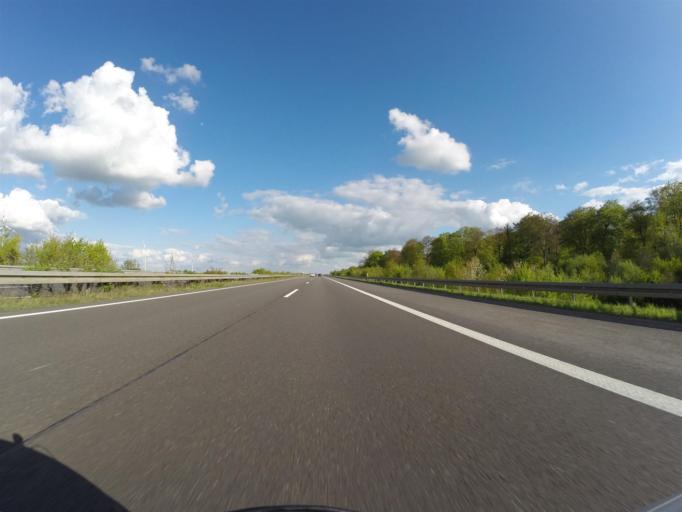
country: DE
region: Saarland
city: Orscholz
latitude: 49.4600
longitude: 6.4756
